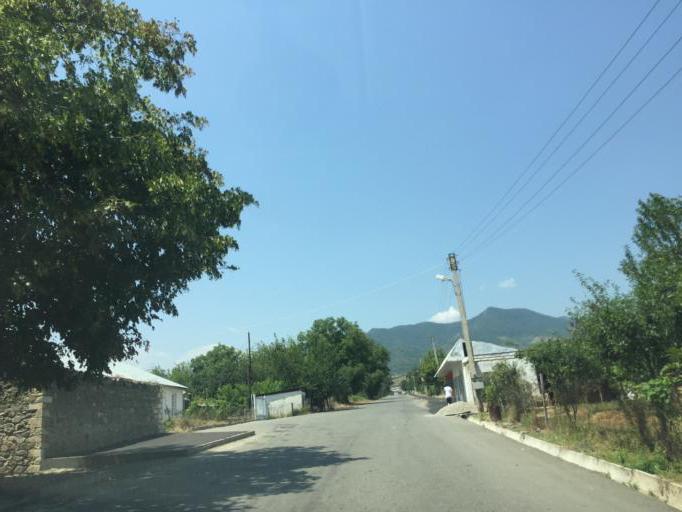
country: AZ
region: Tartar Rayon
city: Martakert
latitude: 40.1292
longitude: 46.4628
